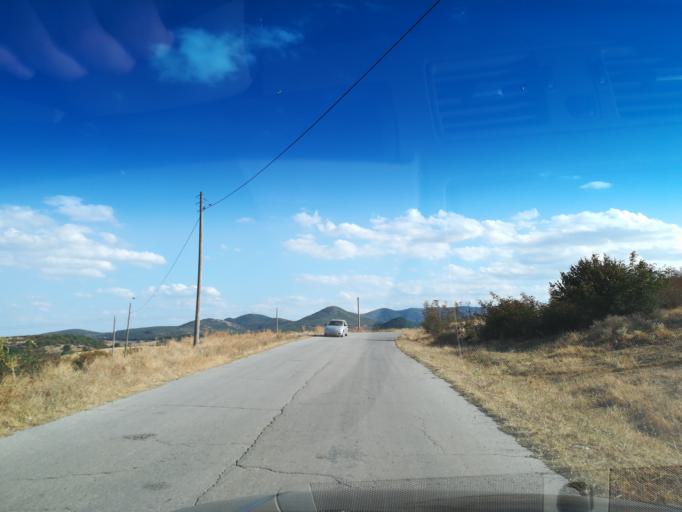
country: BG
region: Khaskovo
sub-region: Obshtina Mineralni Bani
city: Mineralni Bani
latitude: 41.9689
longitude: 25.3007
